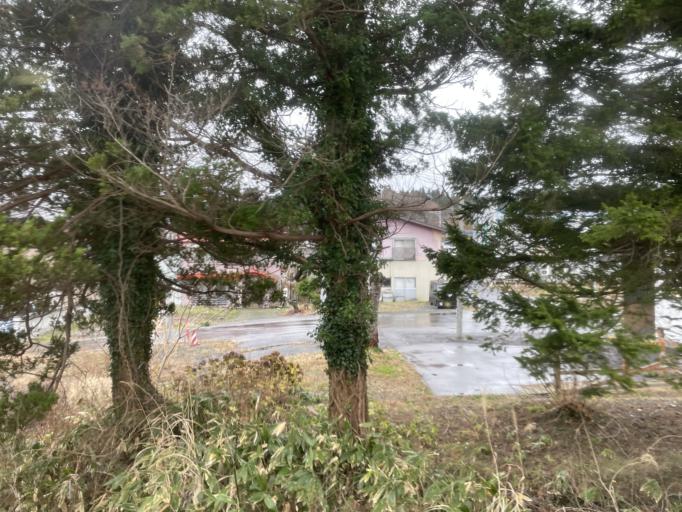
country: JP
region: Aomori
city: Goshogawara
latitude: 41.1794
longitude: 140.4908
